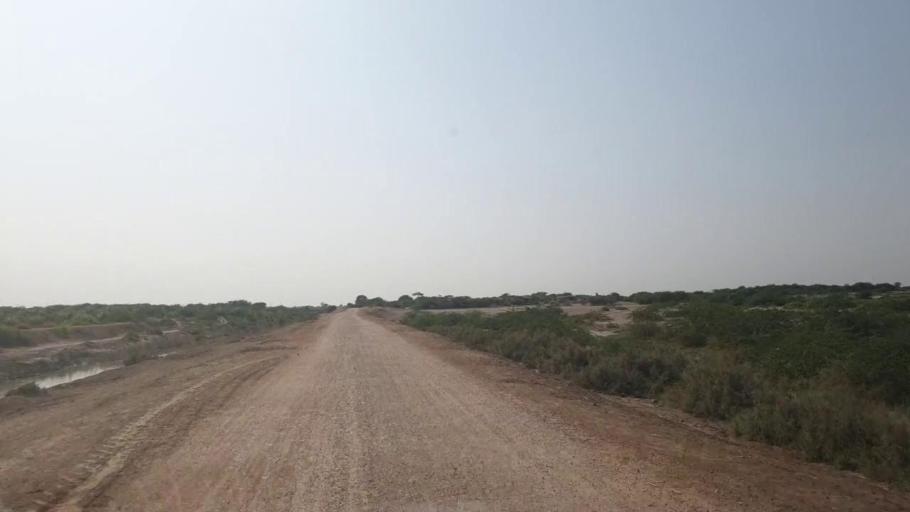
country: PK
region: Sindh
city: Kadhan
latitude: 24.4634
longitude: 68.9051
